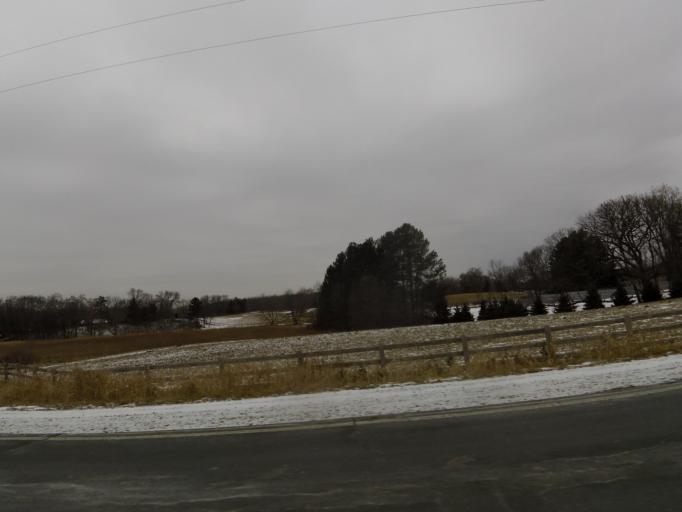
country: US
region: Minnesota
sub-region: Hennepin County
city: Medina
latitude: 45.0267
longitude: -93.5869
